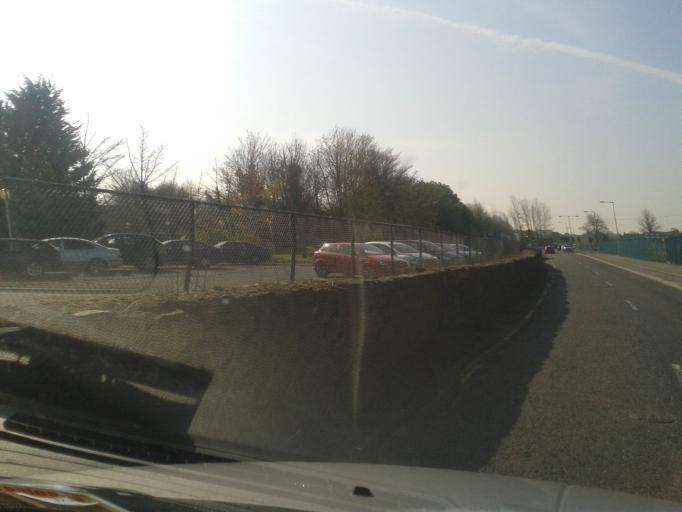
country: IE
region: Leinster
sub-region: Fingal County
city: Swords
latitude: 53.4696
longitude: -6.2202
